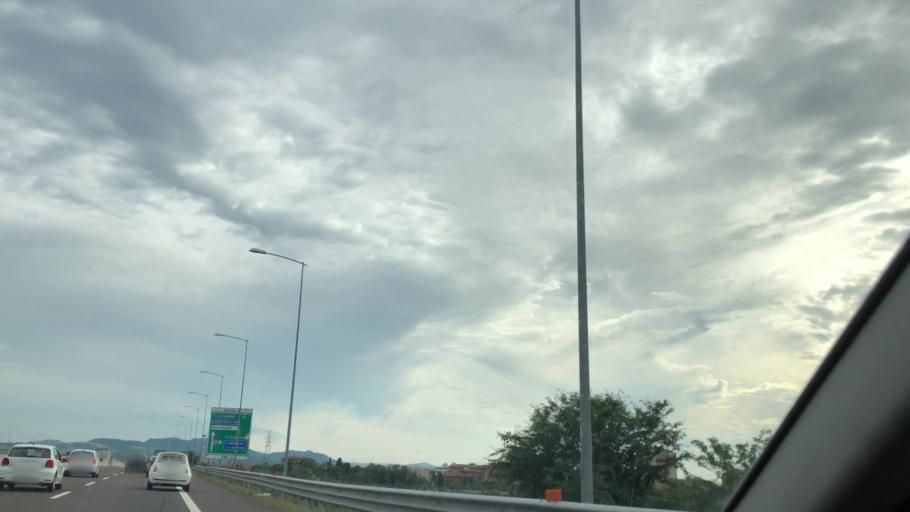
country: IT
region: Emilia-Romagna
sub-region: Provincia di Bologna
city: Calderara di Reno
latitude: 44.5221
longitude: 11.2856
